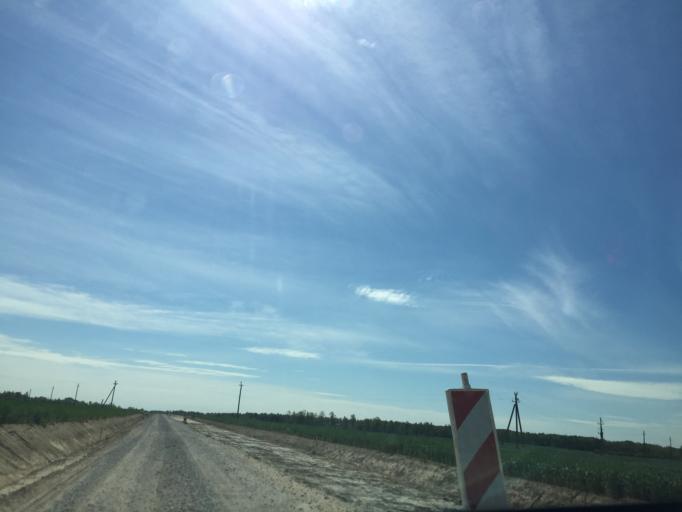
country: LT
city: Linkuva
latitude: 56.0568
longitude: 24.0904
